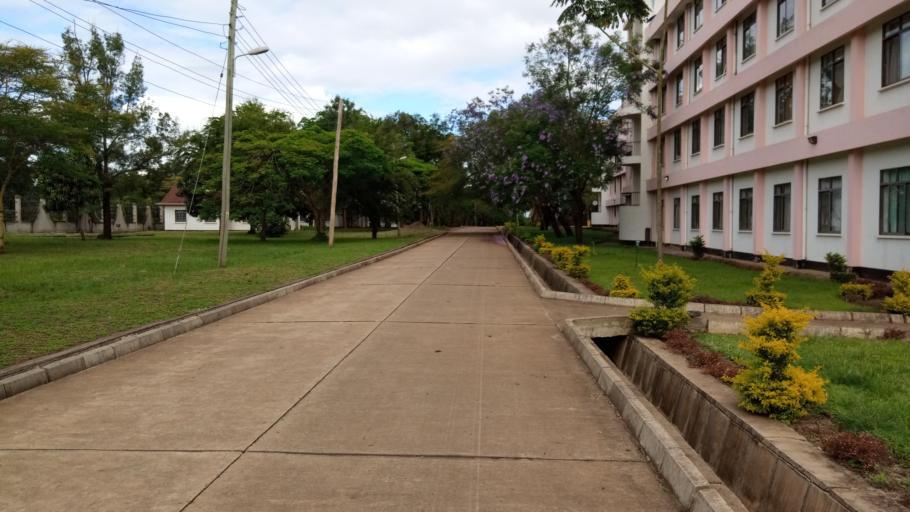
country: TZ
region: Arusha
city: Usa River
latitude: -3.3987
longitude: 36.7987
